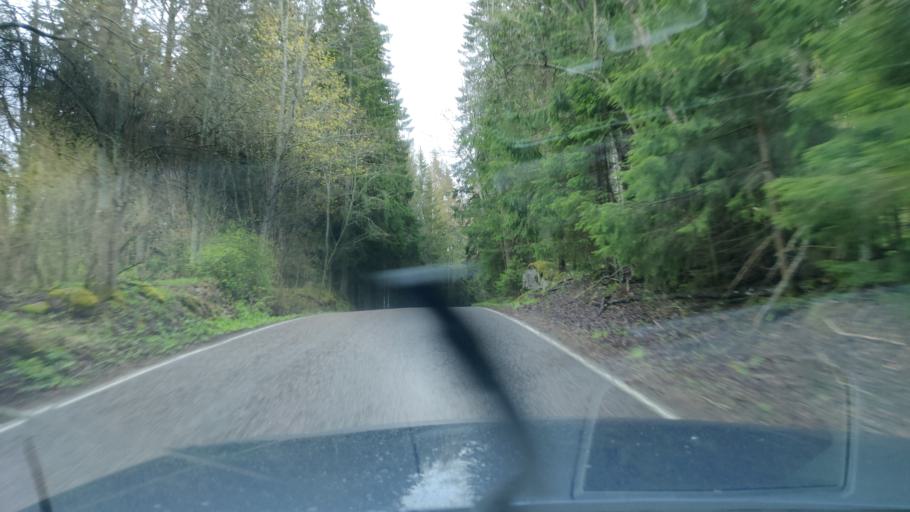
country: FI
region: Uusimaa
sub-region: Helsinki
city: Nurmijaervi
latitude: 60.4930
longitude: 24.7346
